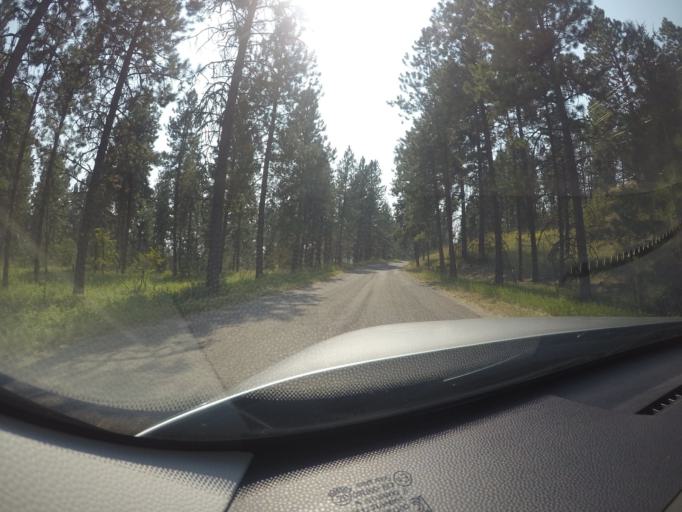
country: US
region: Montana
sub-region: Lake County
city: Polson
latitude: 47.7629
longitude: -114.1607
